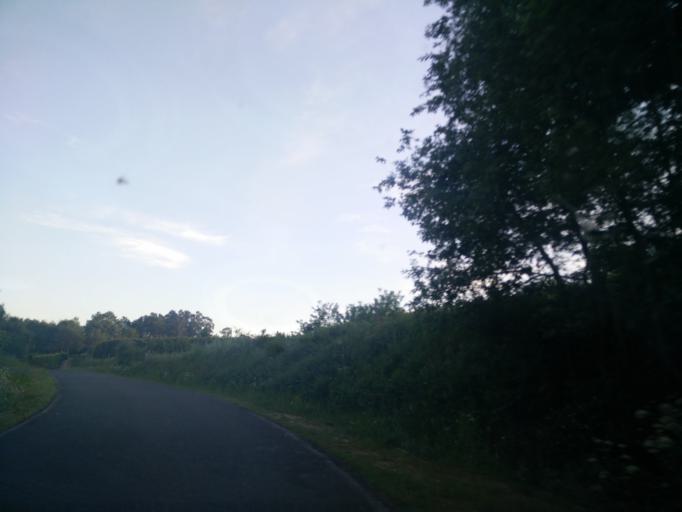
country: ES
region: Galicia
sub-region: Provincia de Pontevedra
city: Mondariz
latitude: 42.2571
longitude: -8.4158
